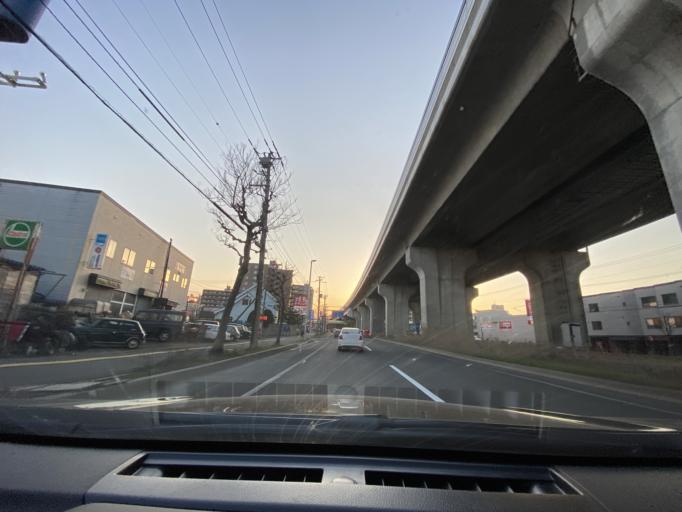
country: JP
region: Hokkaido
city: Sapporo
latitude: 43.1045
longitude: 141.3715
